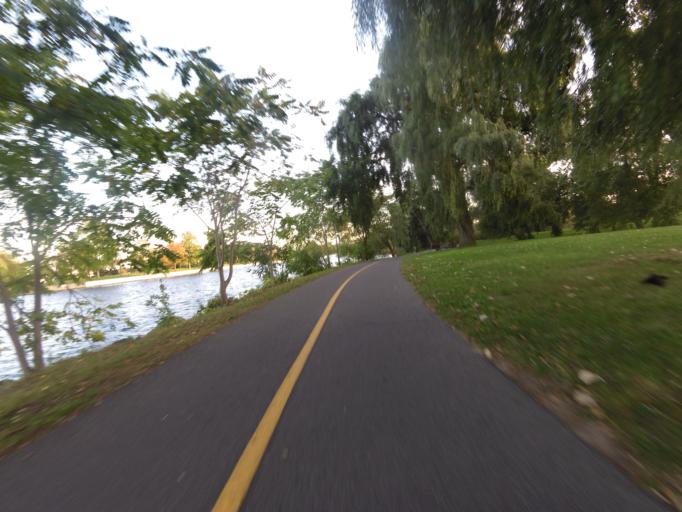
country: CA
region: Ontario
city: Ottawa
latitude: 45.3916
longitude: -75.7015
